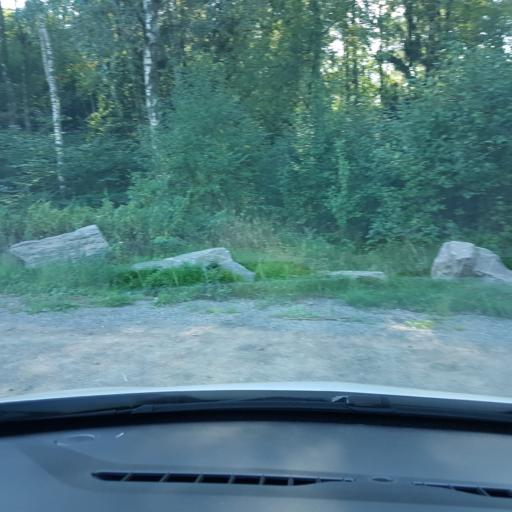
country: SE
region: Vaestra Goetaland
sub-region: Ale Kommun
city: Alafors
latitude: 57.9291
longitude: 12.0947
